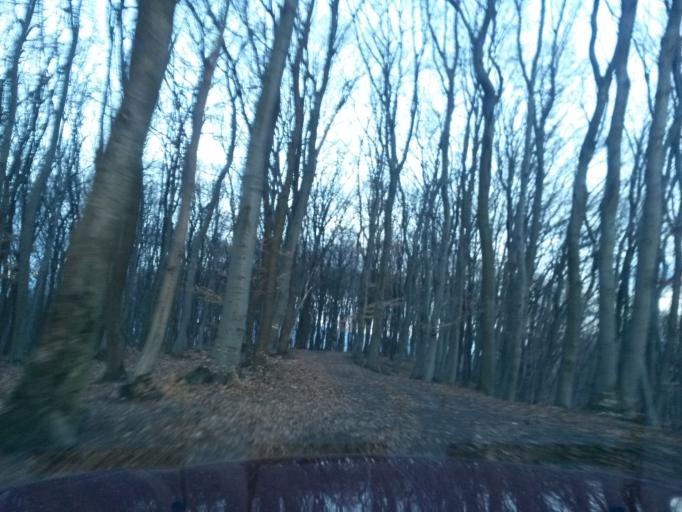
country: SK
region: Kosicky
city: Kosice
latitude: 48.7028
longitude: 21.3800
